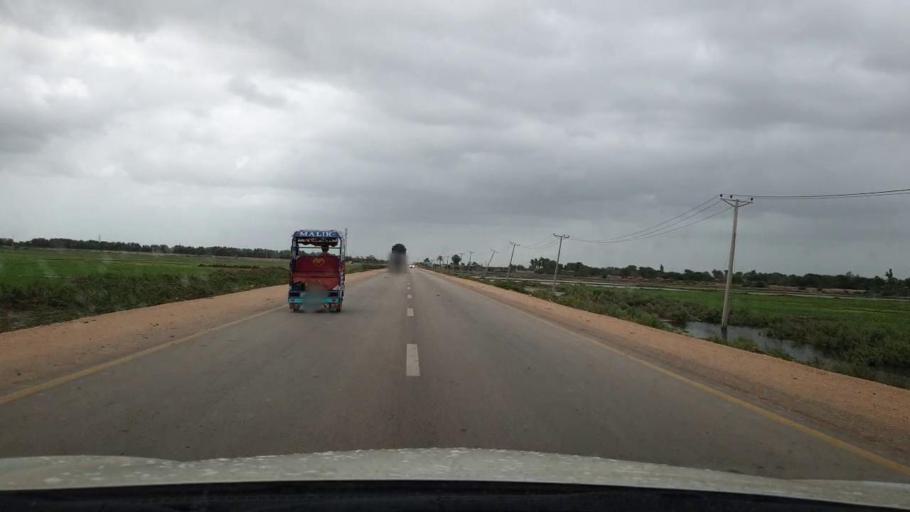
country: PK
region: Sindh
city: Badin
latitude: 24.6556
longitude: 68.7221
